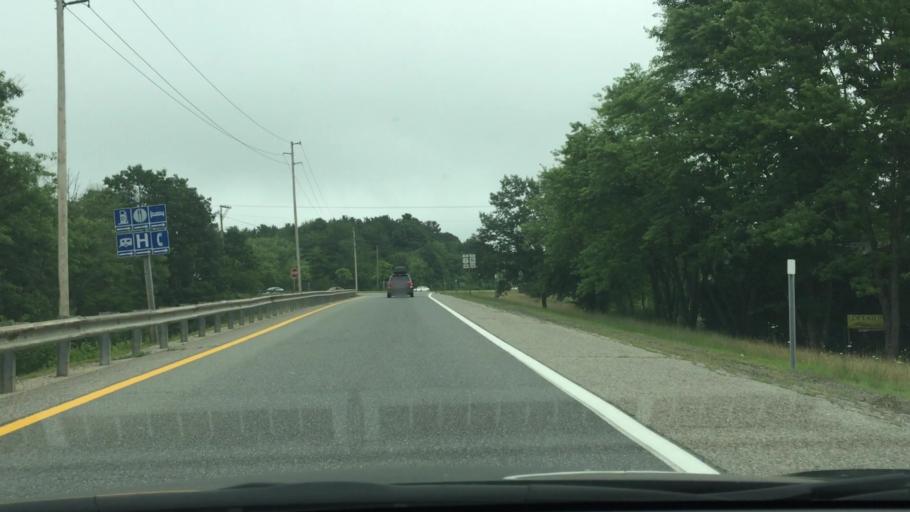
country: US
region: Maine
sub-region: York County
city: York Harbor
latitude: 43.1555
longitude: -70.6655
